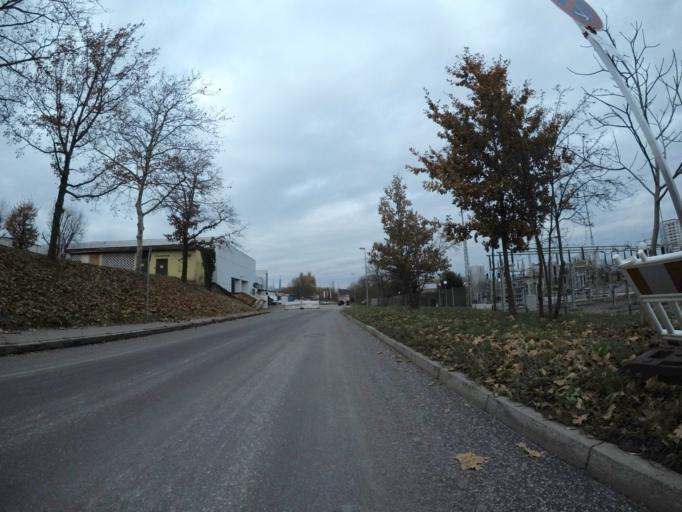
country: DE
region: Baden-Wuerttemberg
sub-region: Tuebingen Region
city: Reutlingen
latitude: 48.5089
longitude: 9.2313
